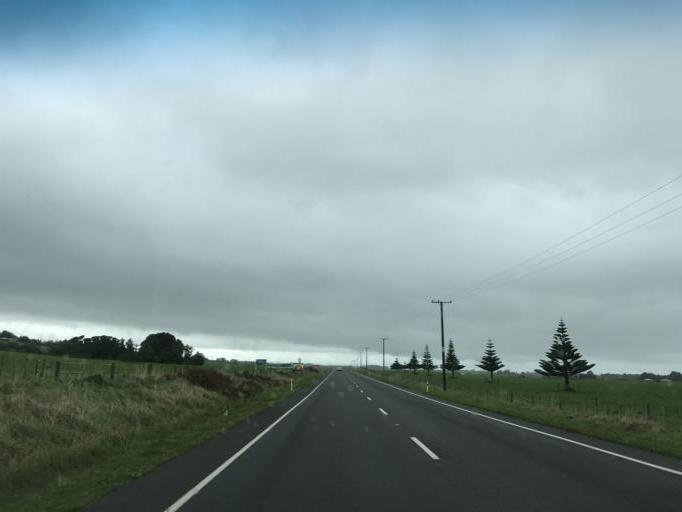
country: NZ
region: Manawatu-Wanganui
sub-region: Wanganui District
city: Wanganui
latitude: -39.8151
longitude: 174.8110
